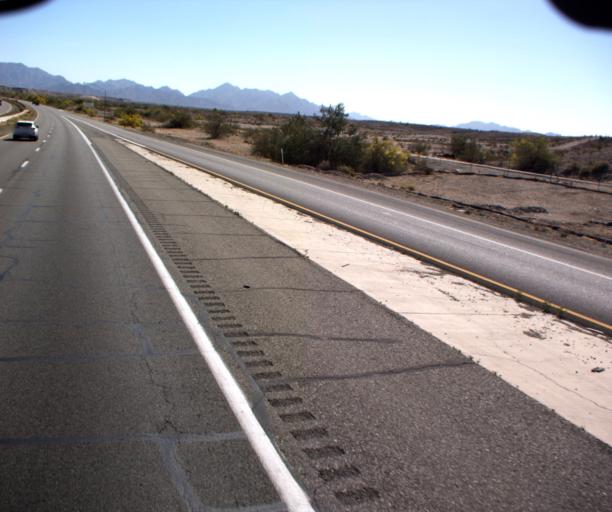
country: US
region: Arizona
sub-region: La Paz County
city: Ehrenberg
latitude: 33.6023
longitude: -114.5161
